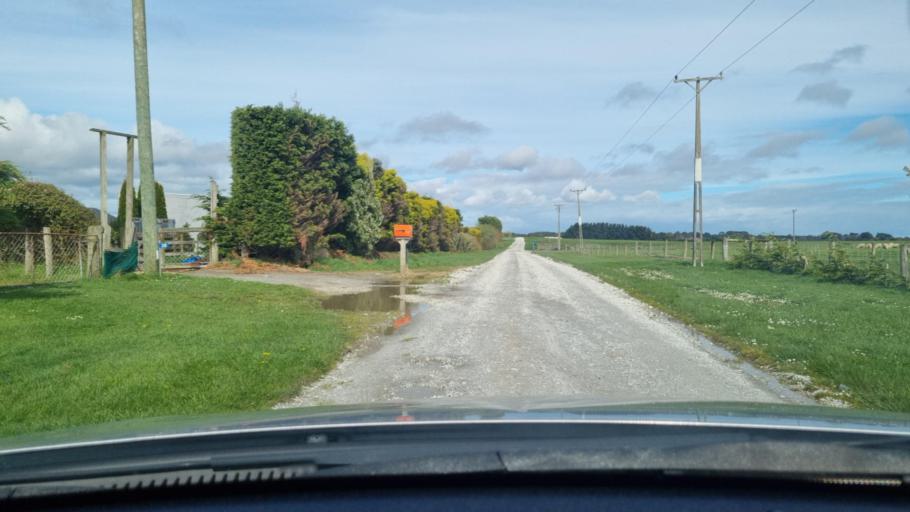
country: NZ
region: Southland
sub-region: Invercargill City
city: Invercargill
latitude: -46.4534
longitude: 168.3832
